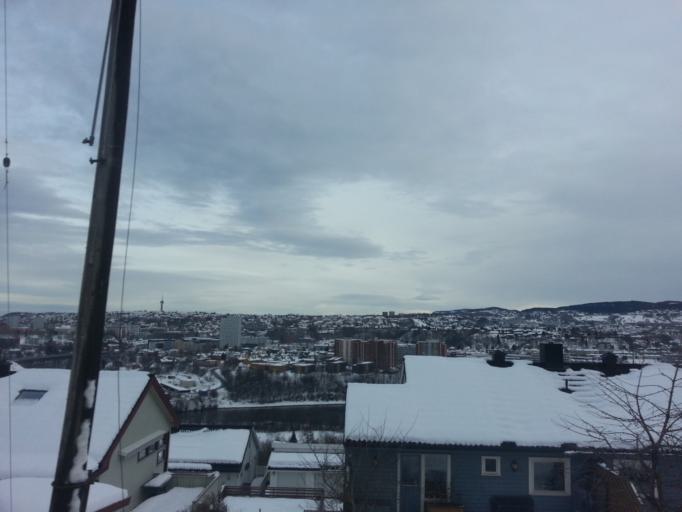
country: NO
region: Sor-Trondelag
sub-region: Trondheim
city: Trondheim
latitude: 63.4062
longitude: 10.3807
